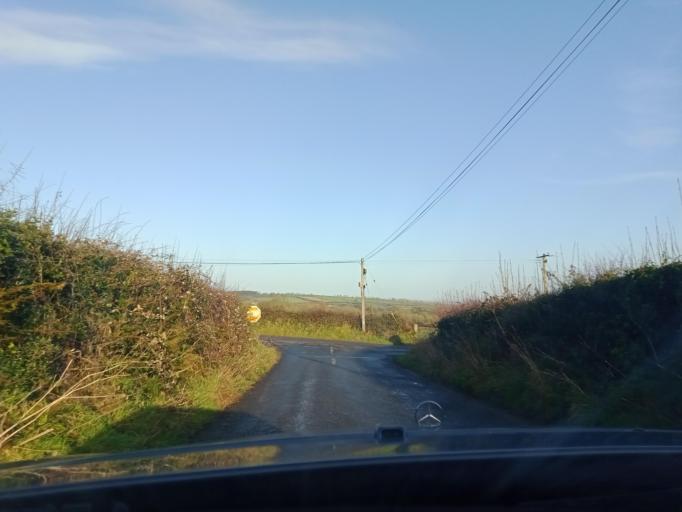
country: IE
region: Leinster
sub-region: Kilkenny
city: Callan
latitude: 52.4662
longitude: -7.4013
